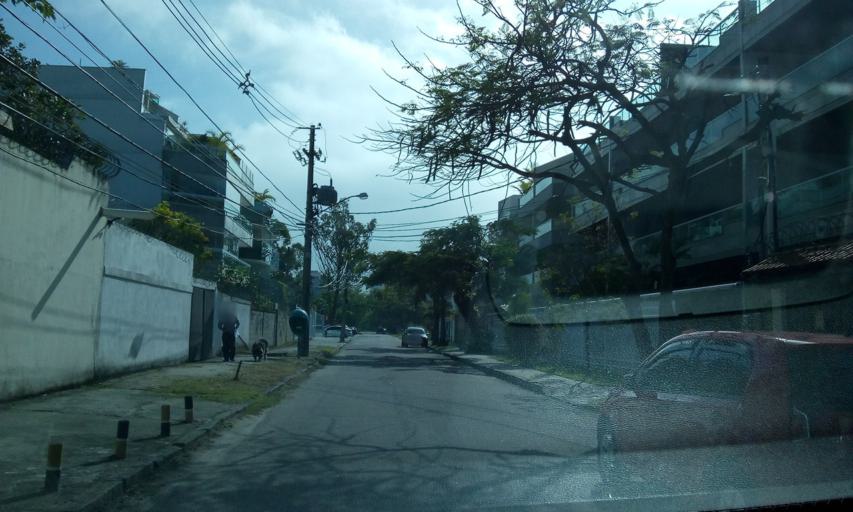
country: BR
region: Rio de Janeiro
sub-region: Nilopolis
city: Nilopolis
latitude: -23.0112
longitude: -43.4474
